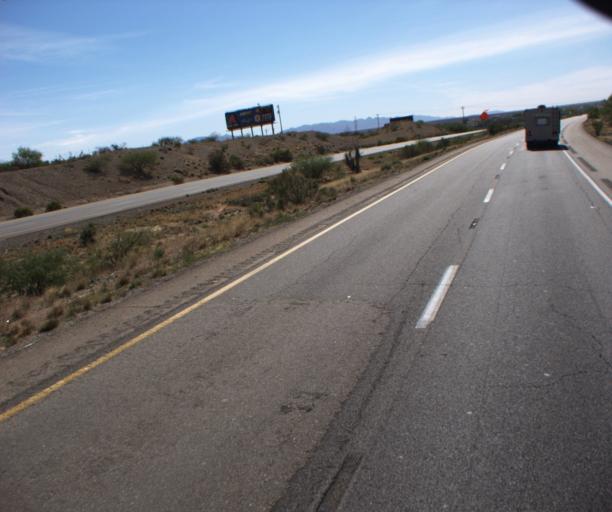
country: US
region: Arizona
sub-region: Cochise County
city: Benson
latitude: 31.9763
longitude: -110.2906
